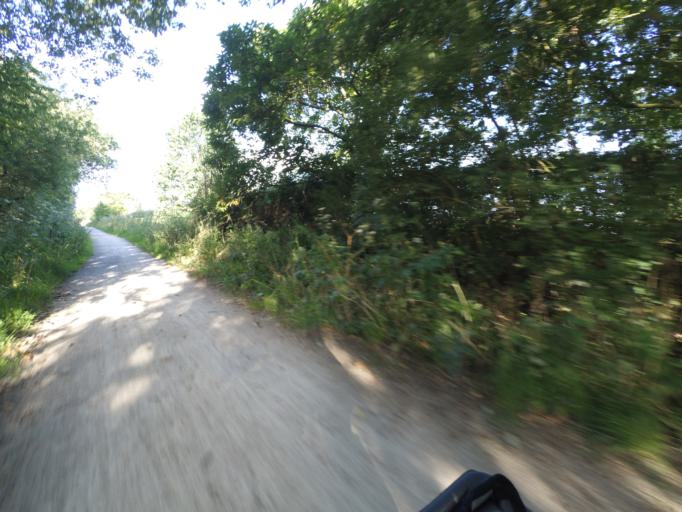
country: GB
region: England
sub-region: Staffordshire
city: Stafford
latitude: 52.7983
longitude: -2.1804
